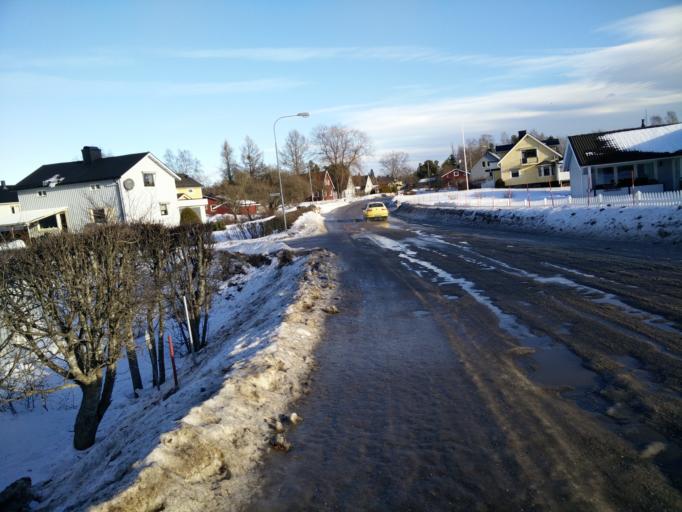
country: SE
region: Vaesternorrland
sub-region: Sundsvalls Kommun
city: Nolby
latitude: 62.2701
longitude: 17.3581
